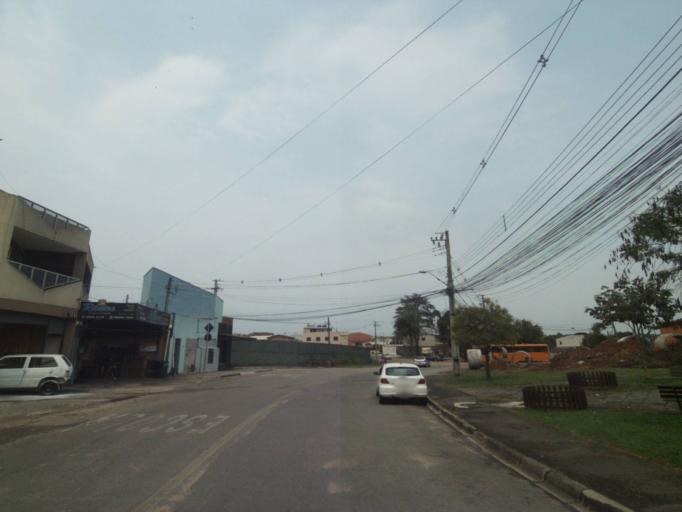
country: BR
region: Parana
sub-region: Curitiba
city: Curitiba
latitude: -25.4821
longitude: -49.3048
